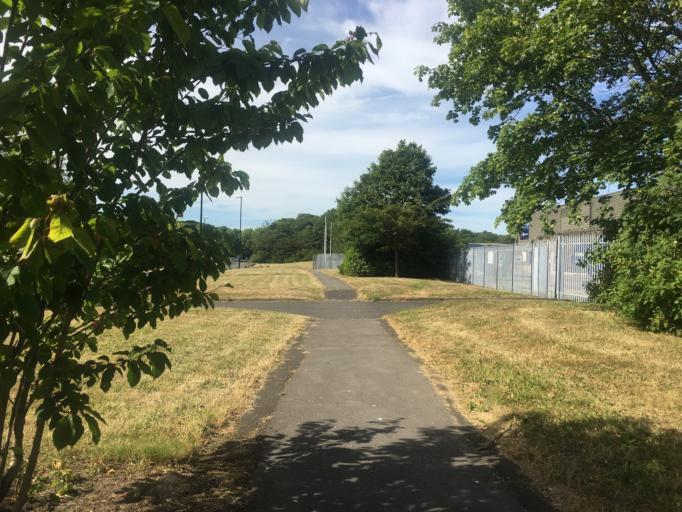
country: GB
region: England
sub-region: Sunderland
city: Washington
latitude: 54.8856
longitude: -1.5388
